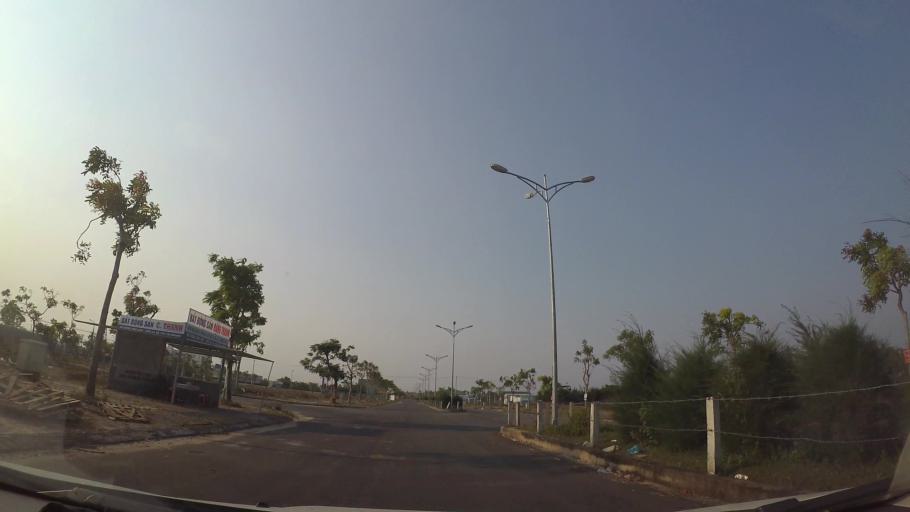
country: VN
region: Da Nang
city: Ngu Hanh Son
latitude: 15.9606
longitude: 108.2614
